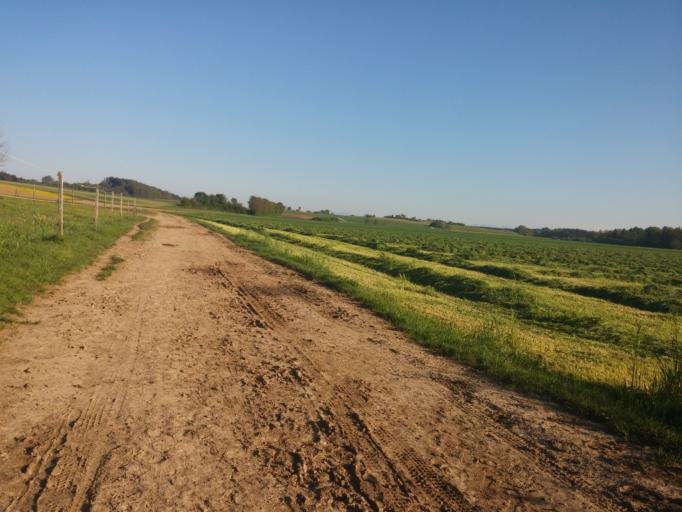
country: DE
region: Bavaria
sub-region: Upper Bavaria
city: Poing
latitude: 48.1451
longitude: 11.8248
